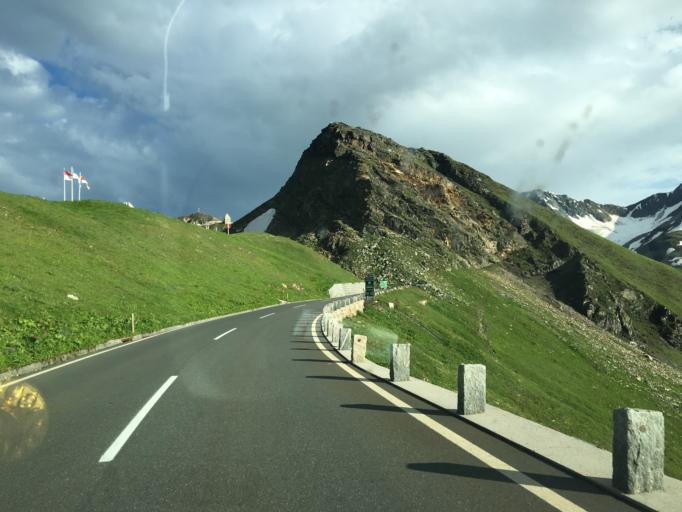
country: AT
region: Carinthia
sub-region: Politischer Bezirk Spittal an der Drau
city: Heiligenblut
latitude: 47.1232
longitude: 12.8200
